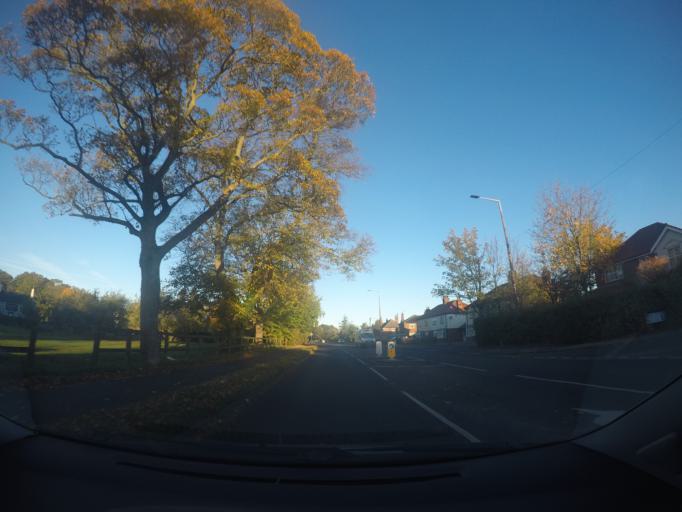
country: GB
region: England
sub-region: City of York
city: York
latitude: 53.9763
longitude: -1.1082
